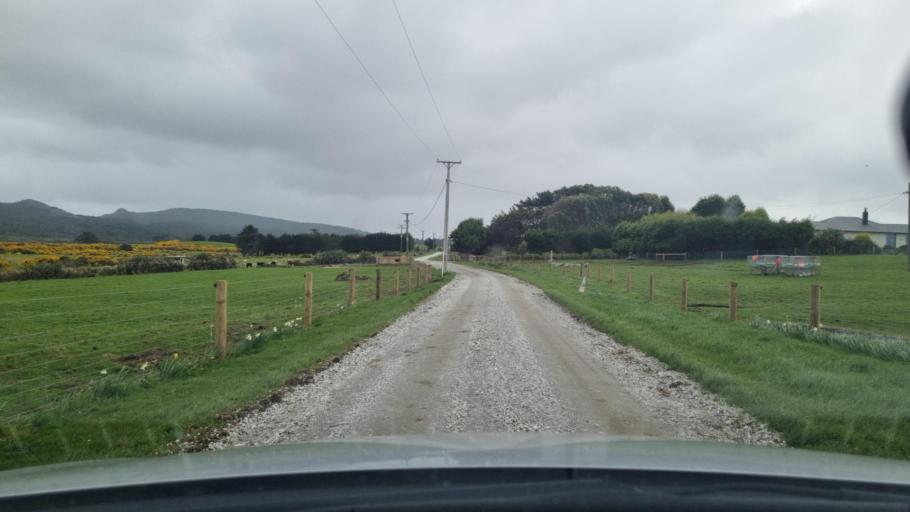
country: NZ
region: Southland
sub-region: Invercargill City
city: Bluff
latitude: -46.5434
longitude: 168.2954
